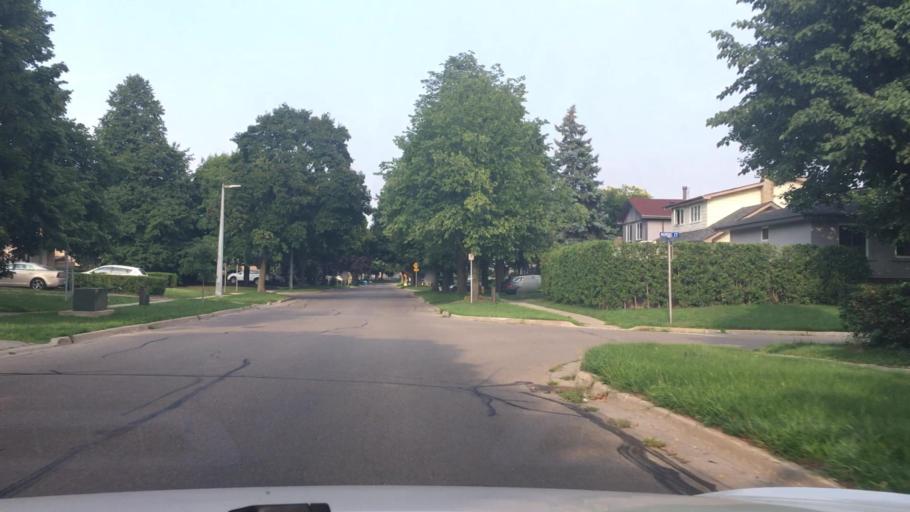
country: CA
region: Ontario
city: Ajax
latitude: 43.8734
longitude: -78.9586
